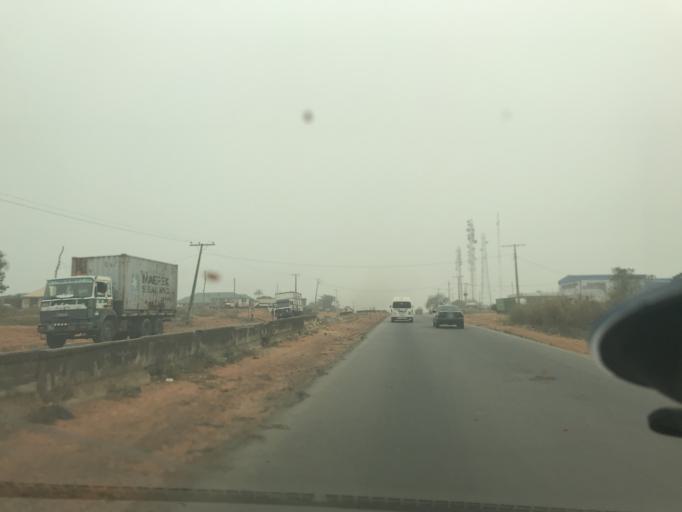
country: NG
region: Ogun
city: Shagamu
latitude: 6.8762
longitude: 3.5894
